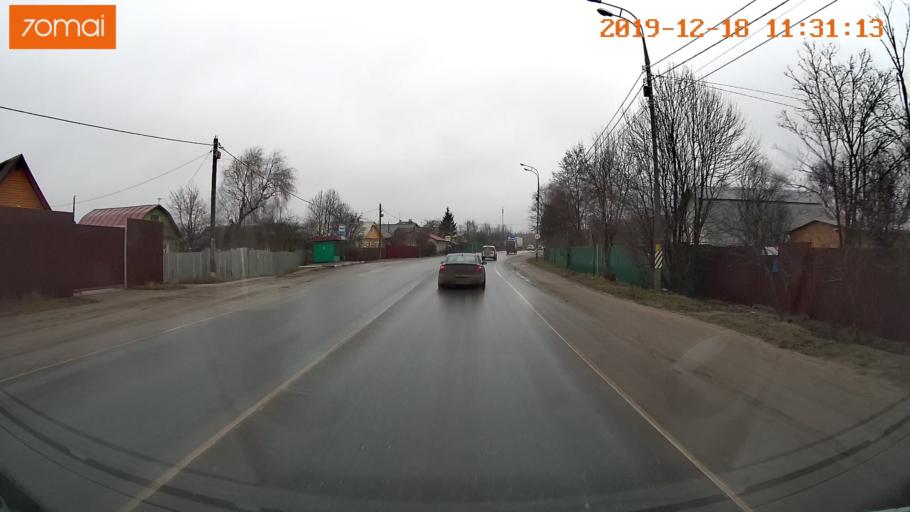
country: RU
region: Moskovskaya
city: Bol'shiye Vyazemy
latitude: 55.6642
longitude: 36.9641
